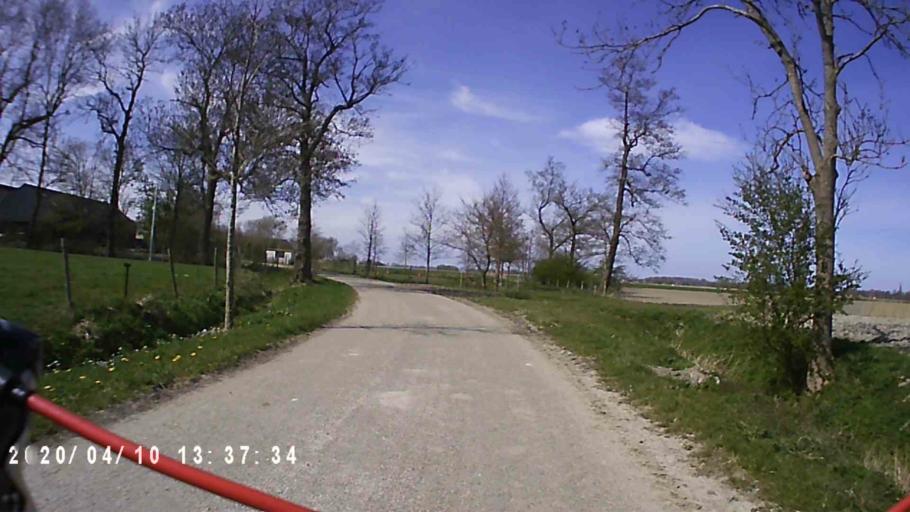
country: NL
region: Groningen
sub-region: Gemeente De Marne
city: Ulrum
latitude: 53.3729
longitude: 6.4016
